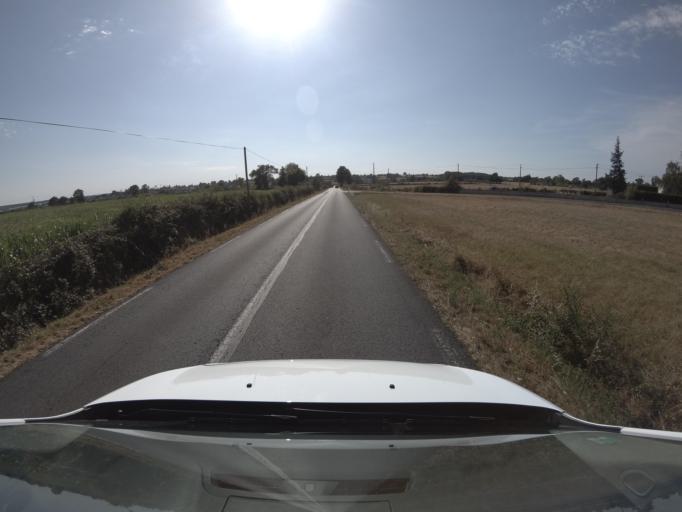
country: FR
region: Poitou-Charentes
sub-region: Departement des Deux-Sevres
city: Argenton-les-Vallees
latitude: 46.9980
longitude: -0.4230
